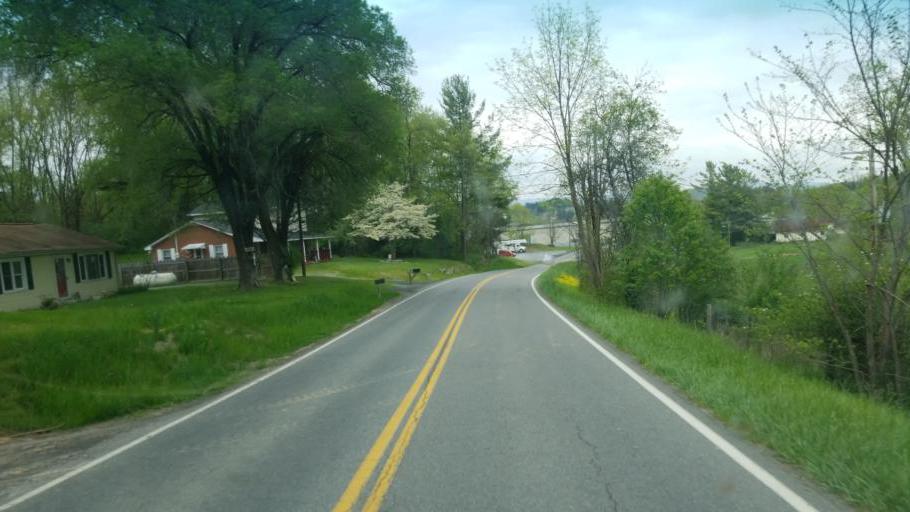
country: US
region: Virginia
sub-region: Smyth County
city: Adwolf
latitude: 36.8063
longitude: -81.5771
